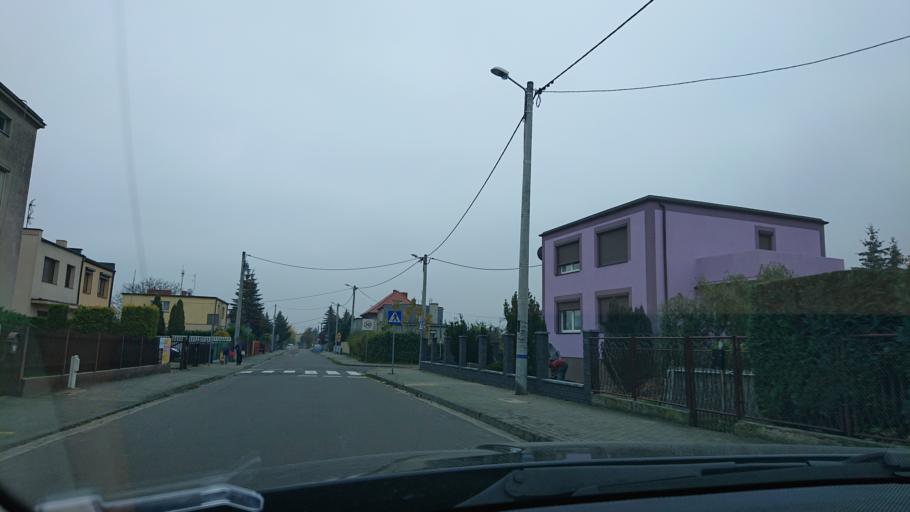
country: PL
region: Greater Poland Voivodeship
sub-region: Powiat gnieznienski
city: Gniezno
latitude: 52.5393
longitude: 17.6237
